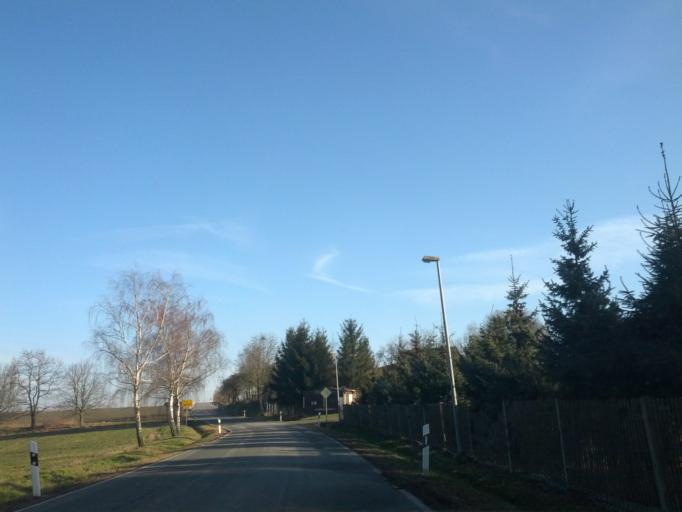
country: DE
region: Thuringia
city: Schonstedt
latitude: 51.0956
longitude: 10.5525
